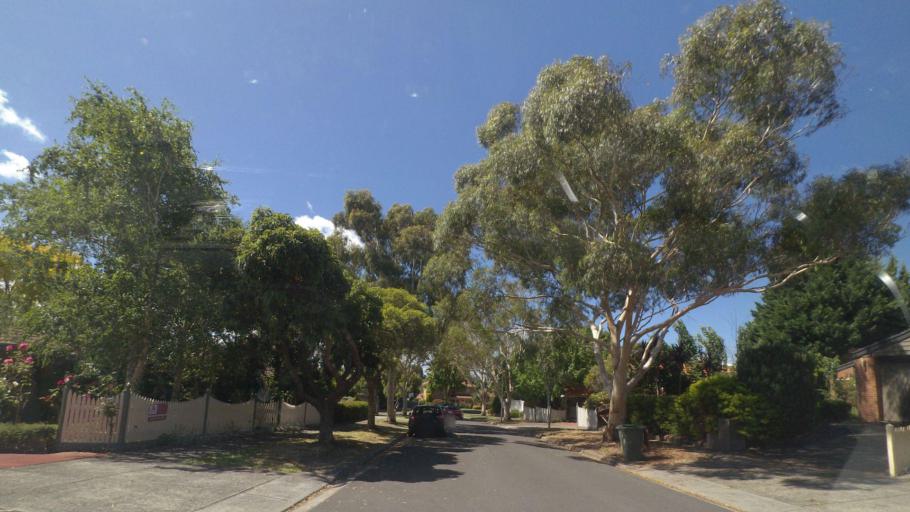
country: AU
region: Victoria
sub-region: Maroondah
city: Croydon Hills
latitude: -37.7720
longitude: 145.2784
